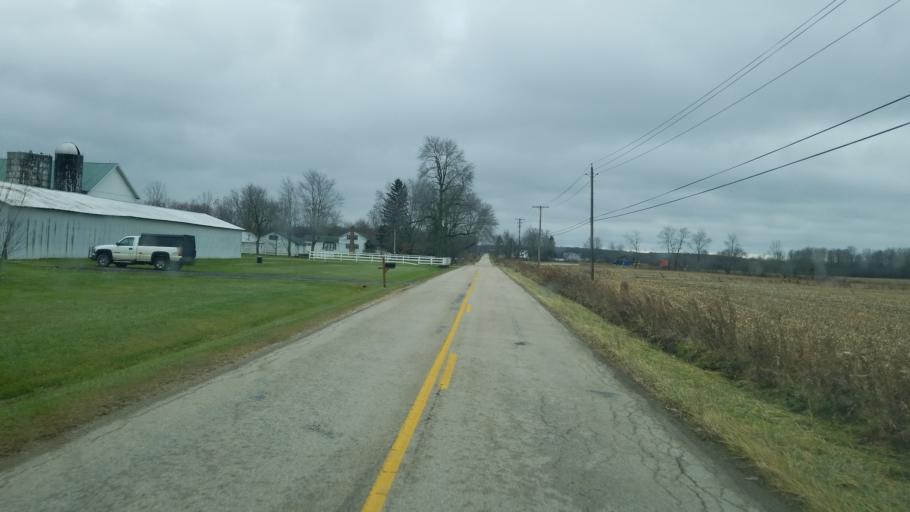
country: US
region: Ohio
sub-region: Ashtabula County
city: Roaming Shores
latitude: 41.6207
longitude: -80.8260
